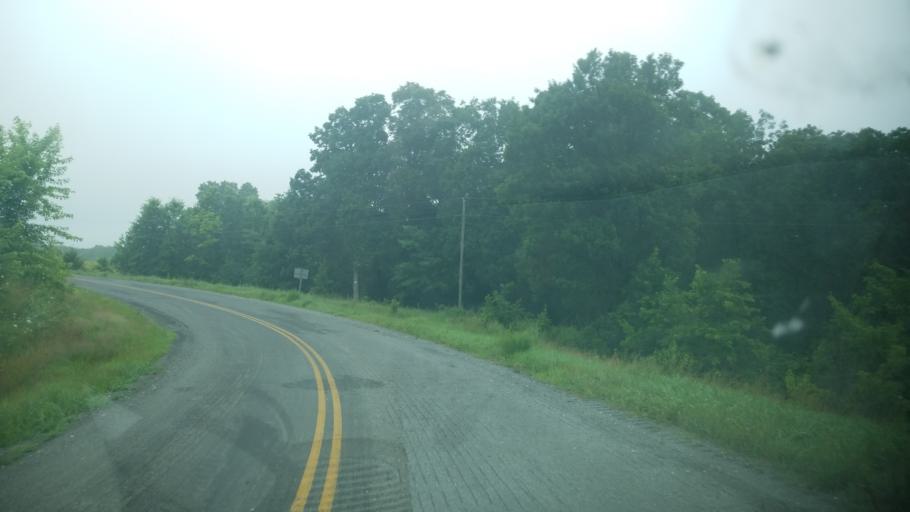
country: US
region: Missouri
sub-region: Audrain County
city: Vandalia
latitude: 39.2873
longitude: -91.3463
